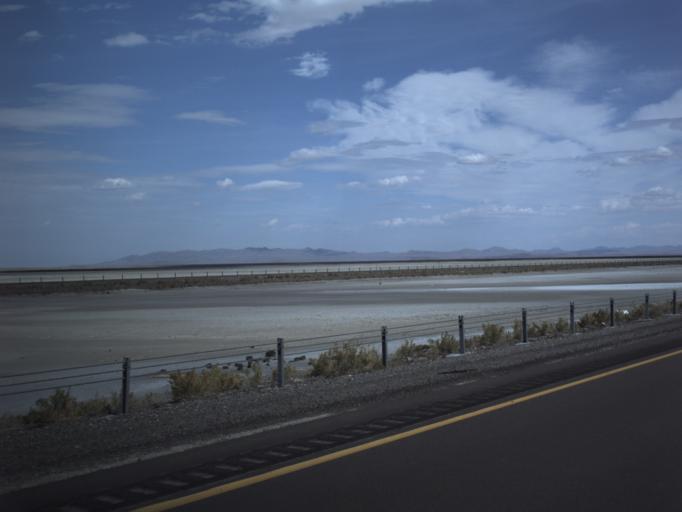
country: US
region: Utah
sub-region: Tooele County
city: Wendover
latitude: 40.7280
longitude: -113.3702
